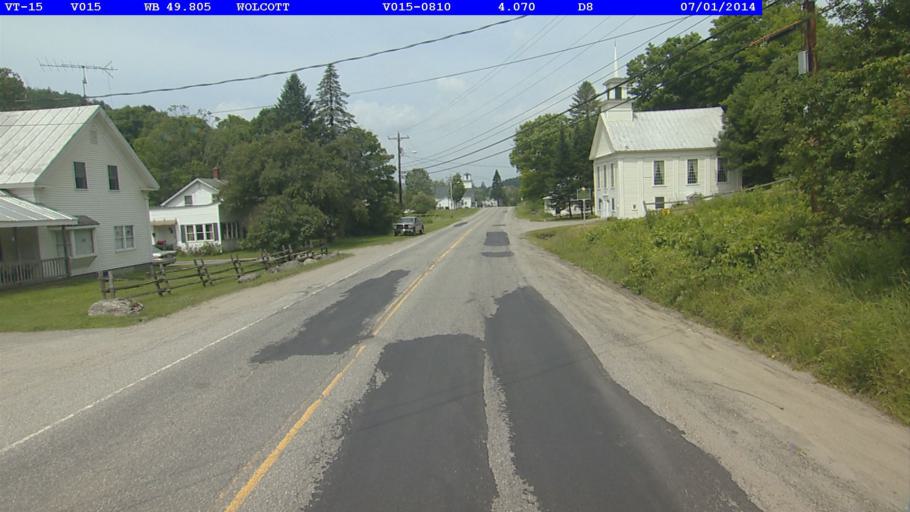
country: US
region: Vermont
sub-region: Caledonia County
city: Hardwick
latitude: 44.5478
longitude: -72.4620
